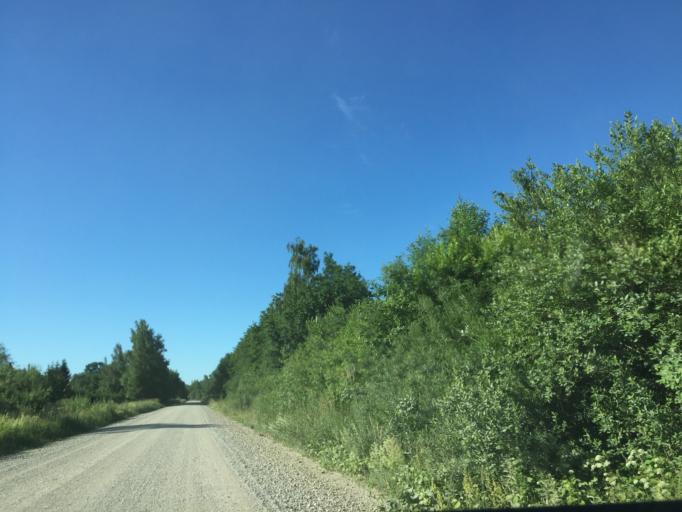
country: LV
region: Ventspils Rajons
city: Piltene
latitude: 57.3209
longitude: 21.6892
